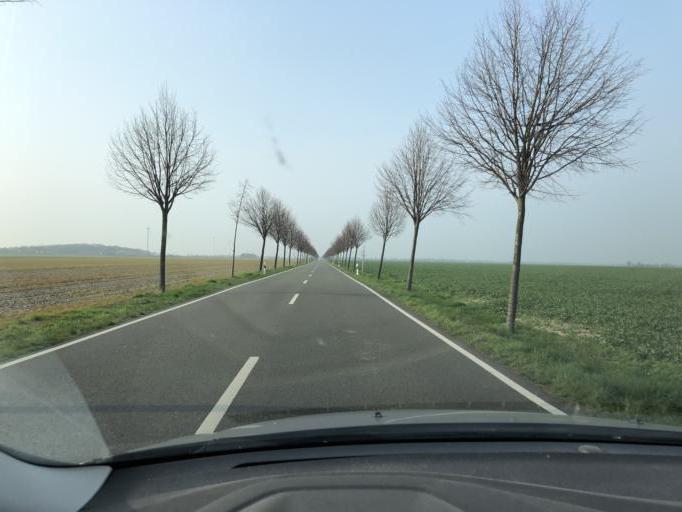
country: DE
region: Saxony-Anhalt
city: Brehna
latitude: 51.5707
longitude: 12.2025
